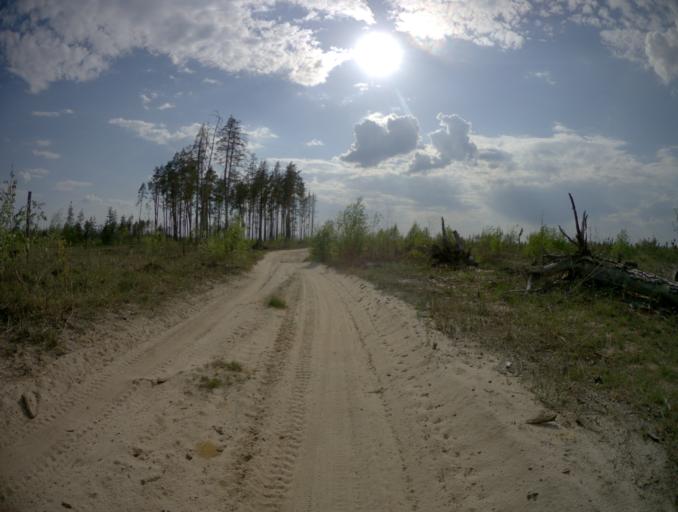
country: RU
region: Ivanovo
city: Talitsy
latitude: 56.4219
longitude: 42.2828
